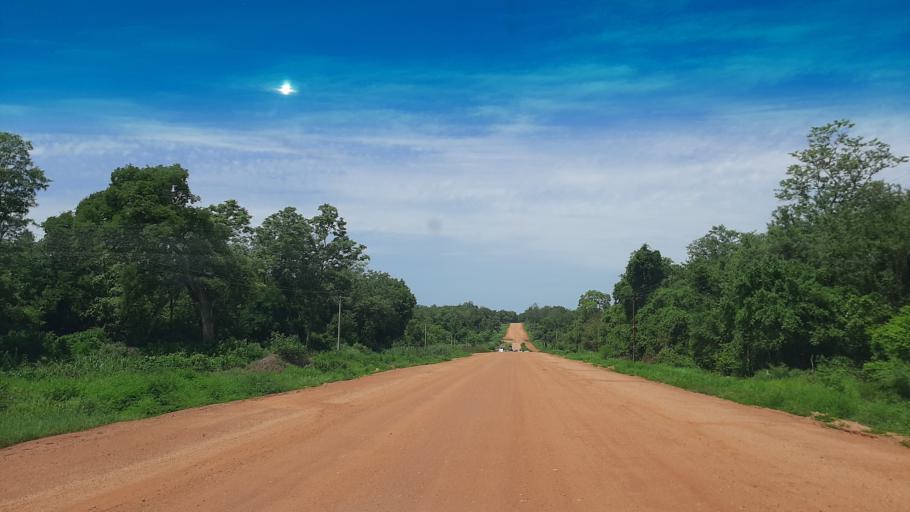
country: ET
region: Gambela
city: Gambela
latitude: 8.0917
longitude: 34.5891
